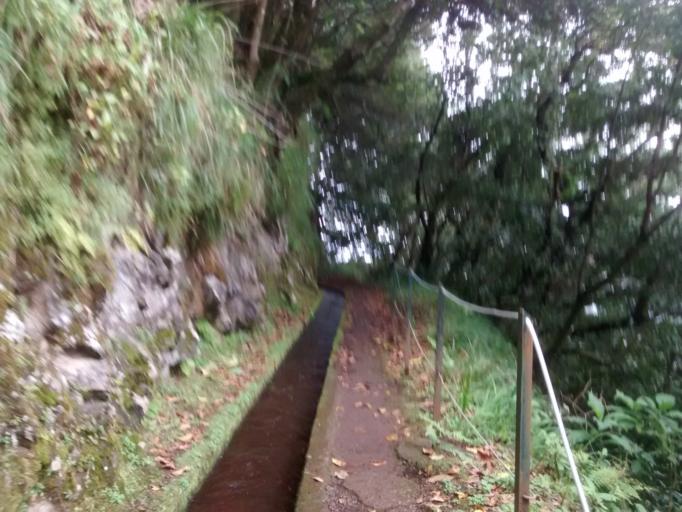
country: PT
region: Madeira
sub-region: Santana
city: Santana
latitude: 32.8095
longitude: -16.9331
